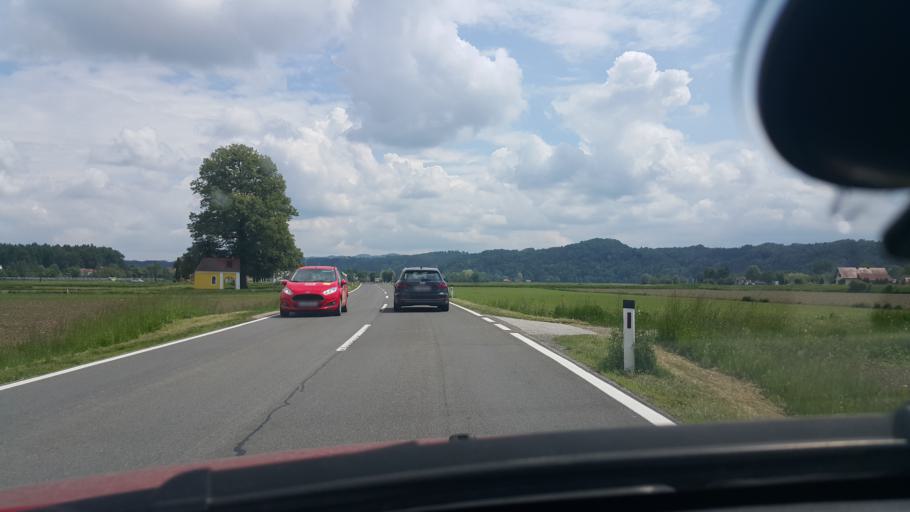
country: AT
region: Styria
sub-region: Politischer Bezirk Deutschlandsberg
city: Sankt Martin im Sulmtal
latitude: 46.7479
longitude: 15.3228
